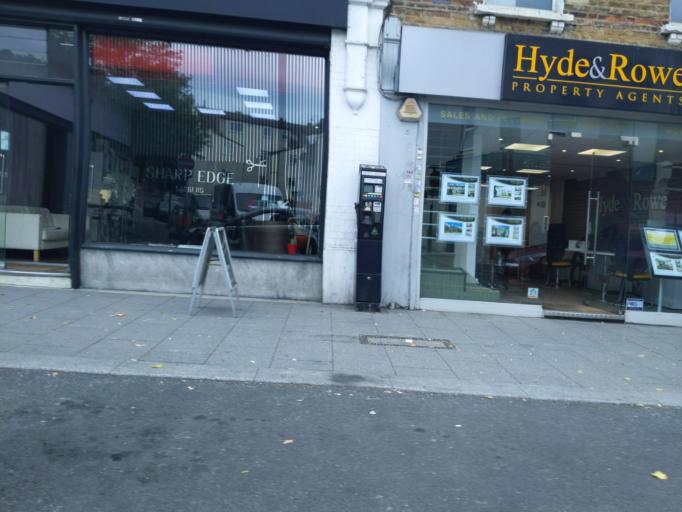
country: GB
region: England
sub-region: Greater London
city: South Croydon
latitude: 51.3632
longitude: -0.0975
